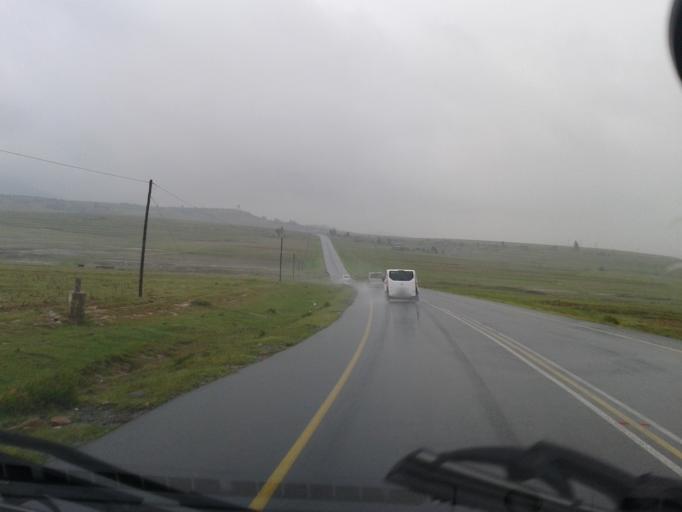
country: LS
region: Mafeteng
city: Mafeteng
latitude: -29.6549
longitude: 27.4567
